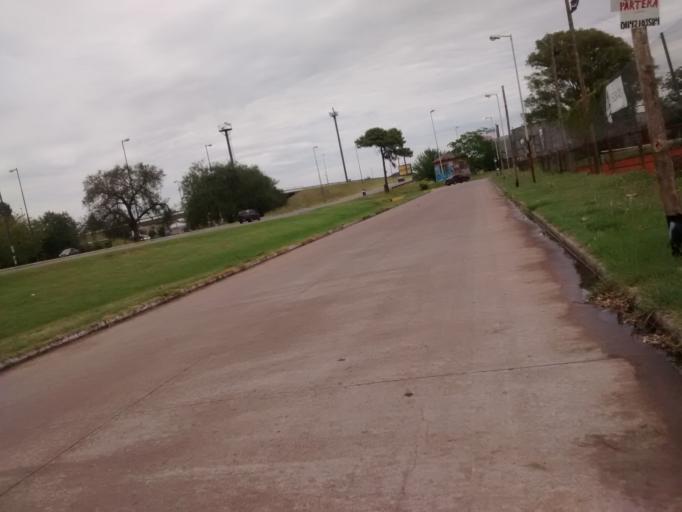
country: AR
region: Buenos Aires
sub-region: Partido de La Plata
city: La Plata
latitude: -34.8970
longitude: -57.9839
